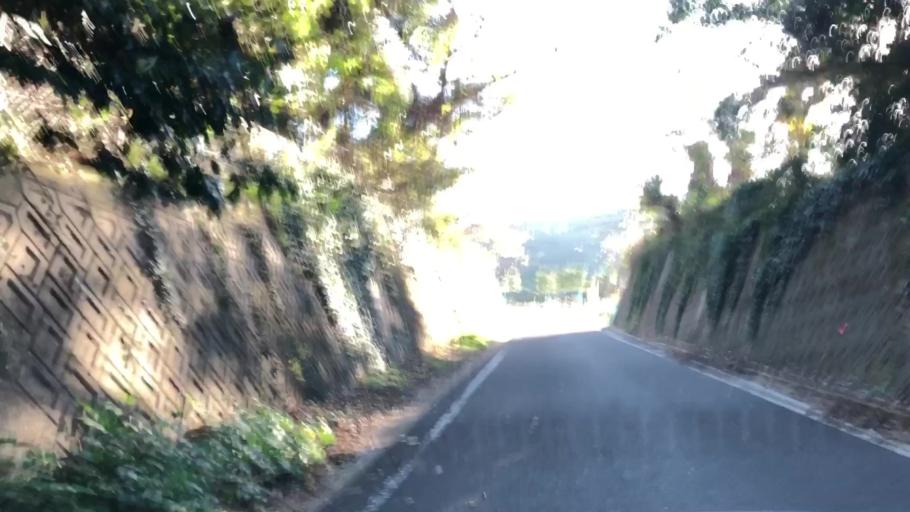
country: JP
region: Nagasaki
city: Sasebo
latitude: 33.0287
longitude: 129.6690
